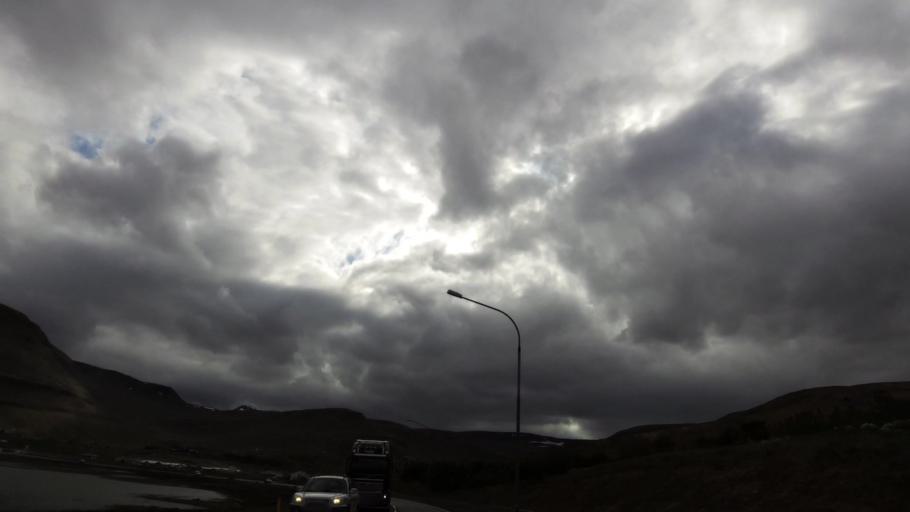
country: IS
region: Westfjords
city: Isafjoerdur
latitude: 66.0649
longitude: -23.1708
